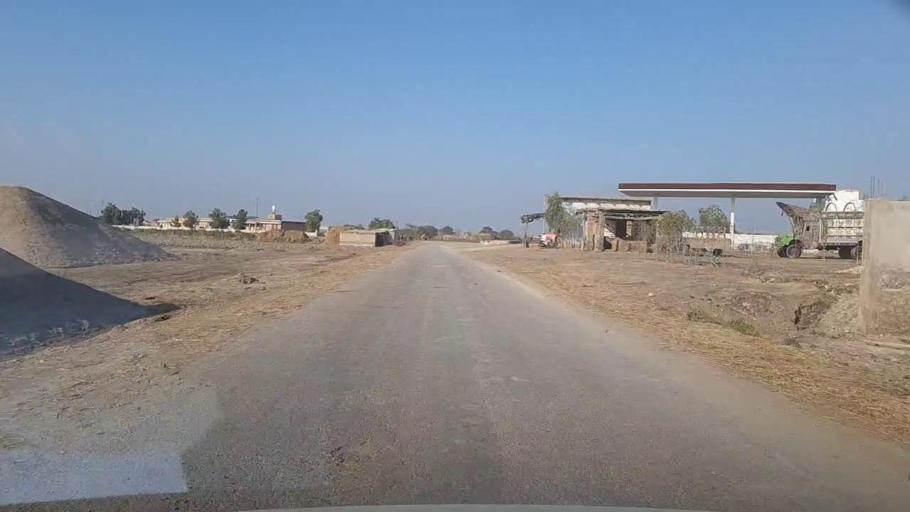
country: PK
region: Sindh
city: Phulji
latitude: 26.8564
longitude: 67.7937
